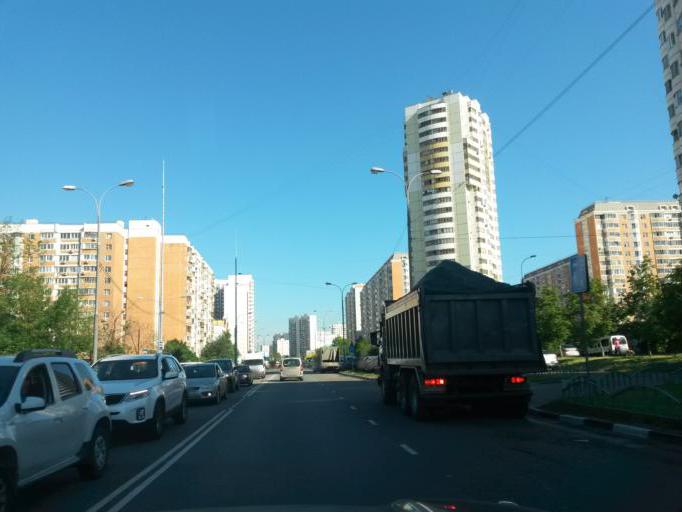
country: RU
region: Moscow
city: Lyublino
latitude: 55.6627
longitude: 37.7727
